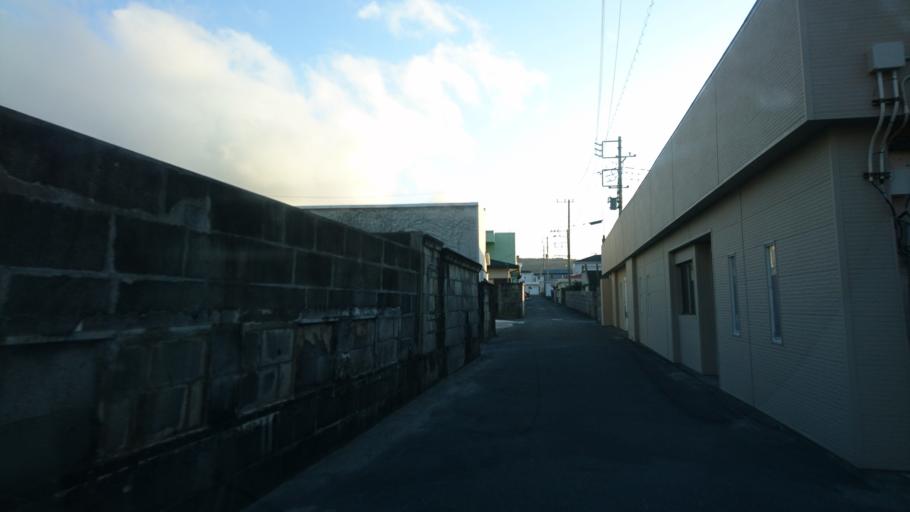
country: JP
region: Shizuoka
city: Shimoda
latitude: 34.3787
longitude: 139.2547
